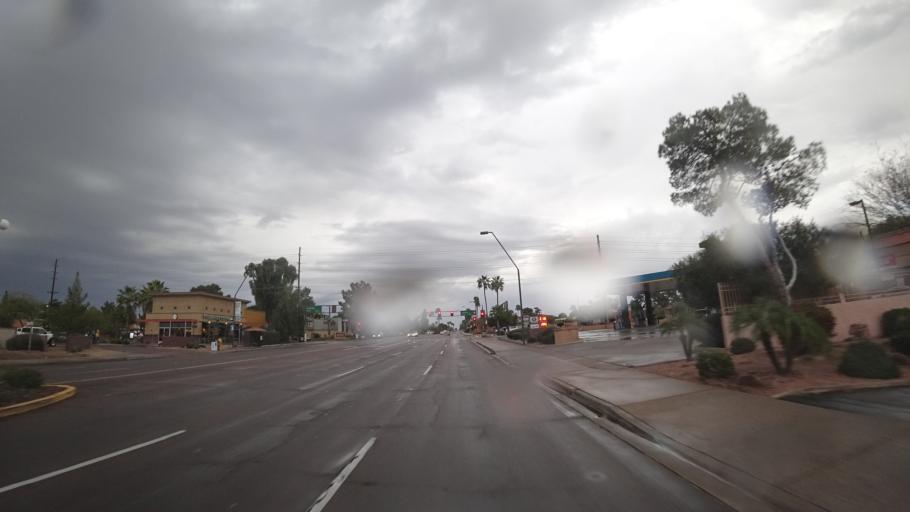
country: US
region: Arizona
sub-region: Maricopa County
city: Tempe
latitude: 33.4504
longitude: -111.9263
